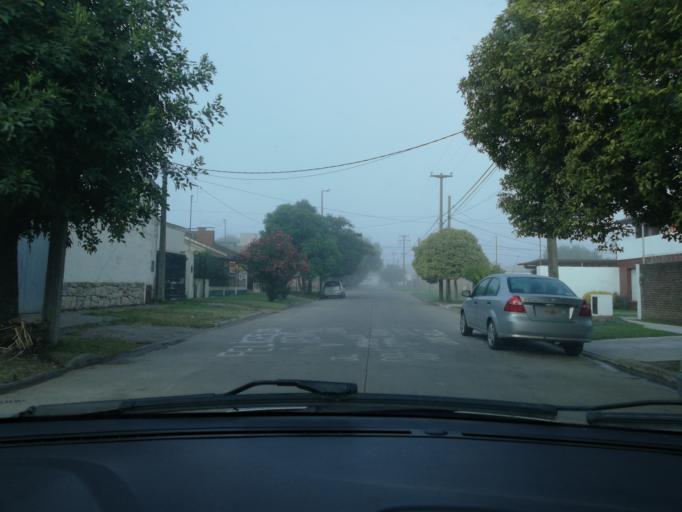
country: AR
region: Buenos Aires
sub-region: Partido de Balcarce
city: Balcarce
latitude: -37.8559
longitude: -58.2634
